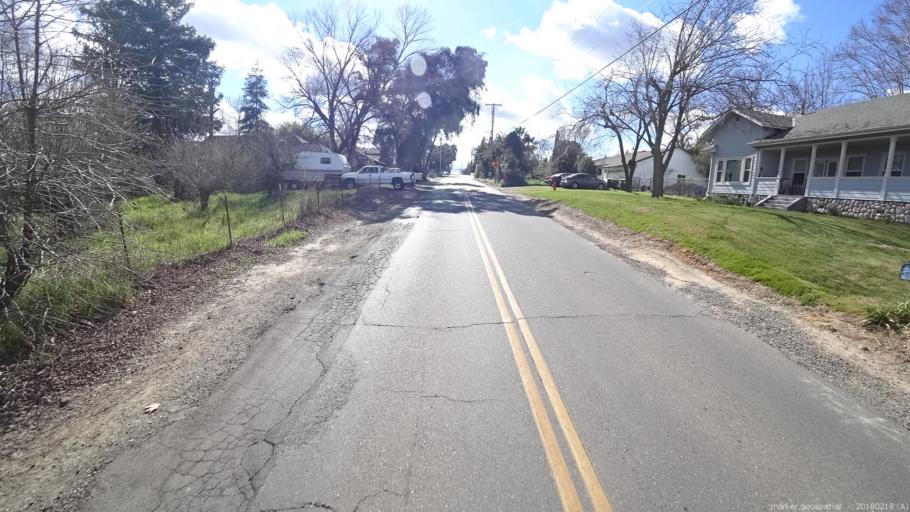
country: US
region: California
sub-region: Sacramento County
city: Orangevale
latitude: 38.6876
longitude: -121.2161
